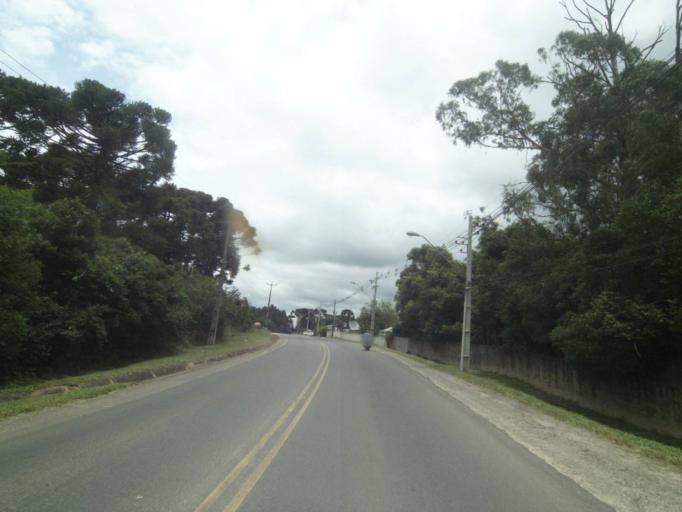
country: BR
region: Parana
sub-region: Campina Grande Do Sul
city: Campina Grande do Sul
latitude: -25.3106
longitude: -49.0670
